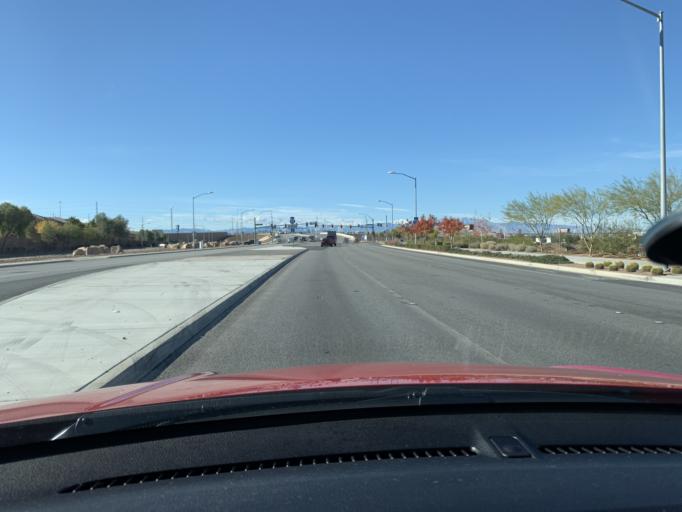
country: US
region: Nevada
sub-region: Clark County
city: Whitney
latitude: 36.0711
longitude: -115.0305
